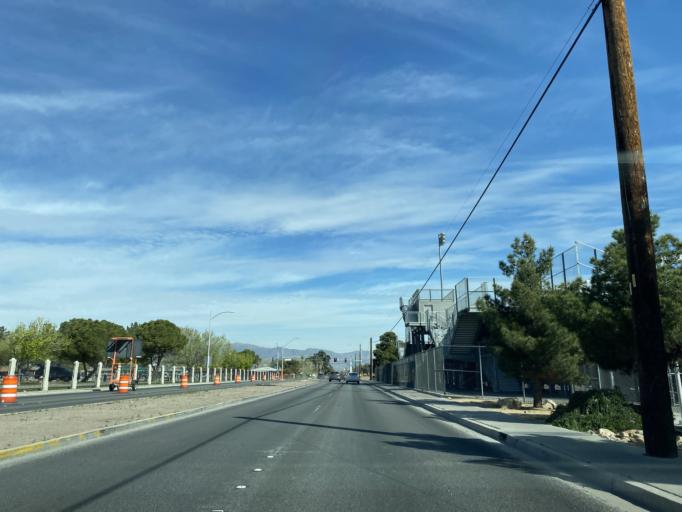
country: US
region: Nevada
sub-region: Clark County
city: North Las Vegas
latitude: 36.1869
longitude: -115.1250
